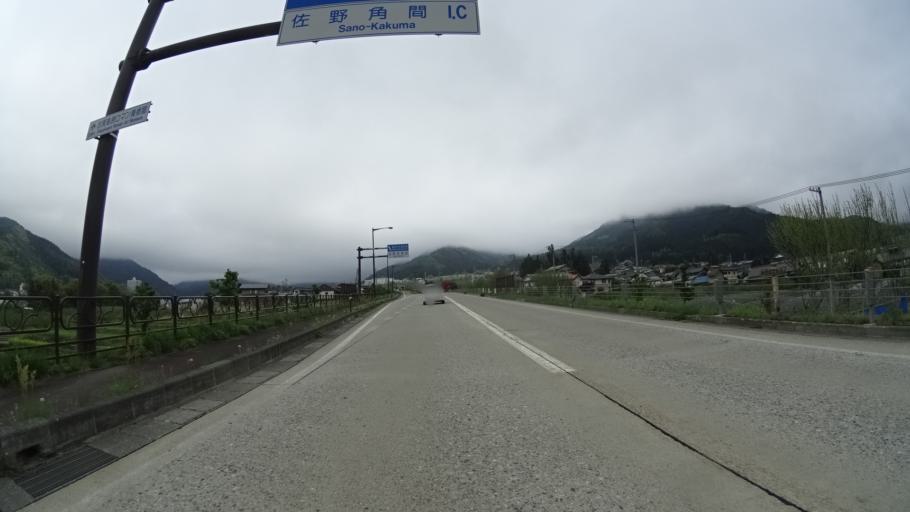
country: JP
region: Nagano
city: Nakano
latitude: 36.7371
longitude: 138.4107
